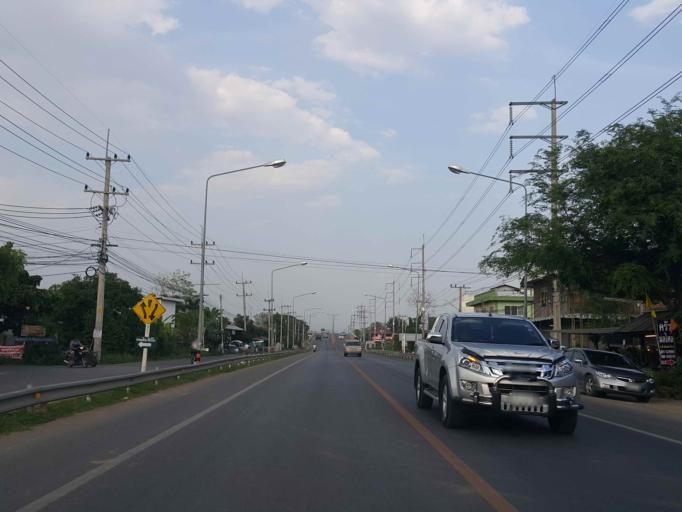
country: TH
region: Chiang Mai
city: San Sai
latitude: 18.9168
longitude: 98.9657
